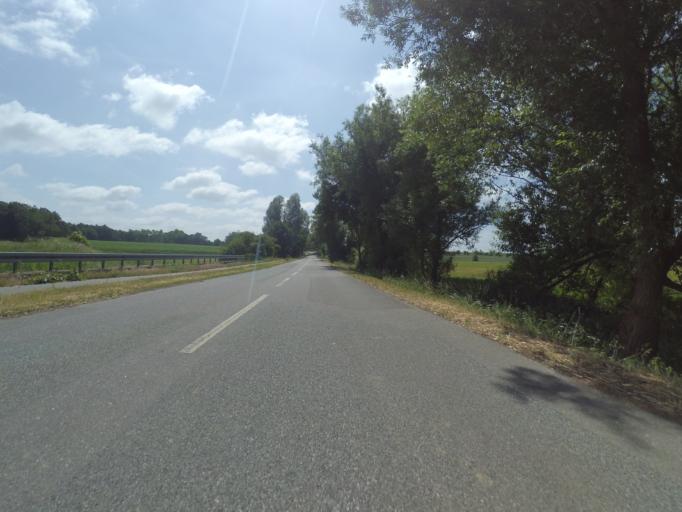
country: DE
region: Mecklenburg-Vorpommern
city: Neuburg
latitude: 53.4663
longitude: 11.9434
